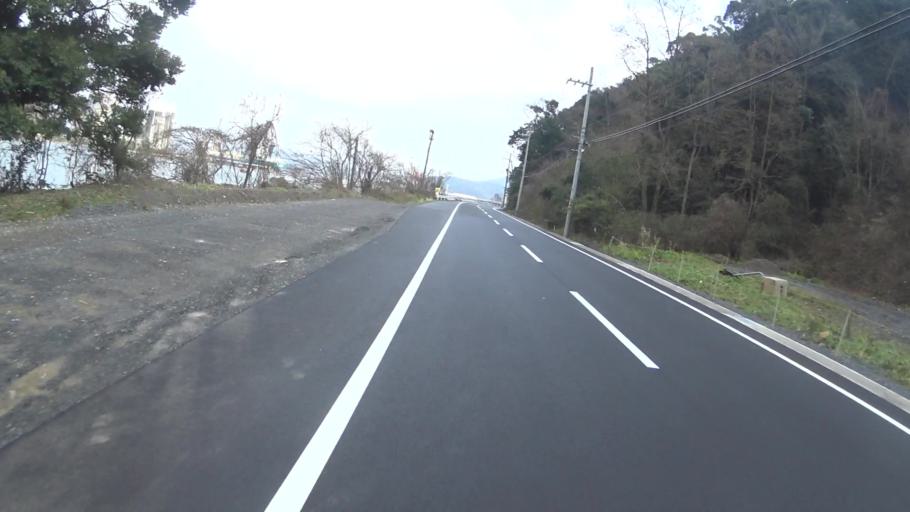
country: JP
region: Kyoto
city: Maizuru
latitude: 35.4710
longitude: 135.3155
